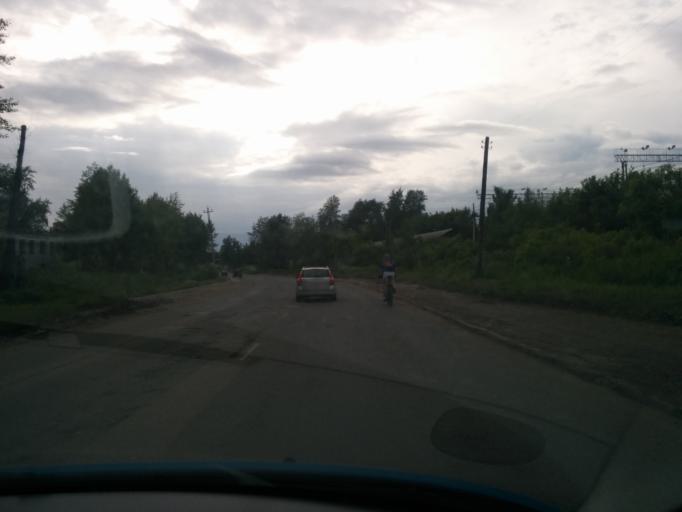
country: RU
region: Perm
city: Perm
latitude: 58.0029
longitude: 56.1902
